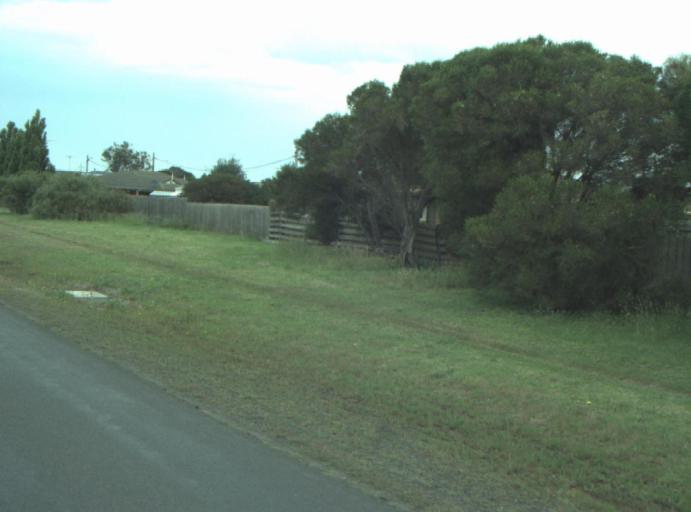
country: AU
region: Victoria
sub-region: Greater Geelong
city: Breakwater
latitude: -38.1882
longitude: 144.3998
